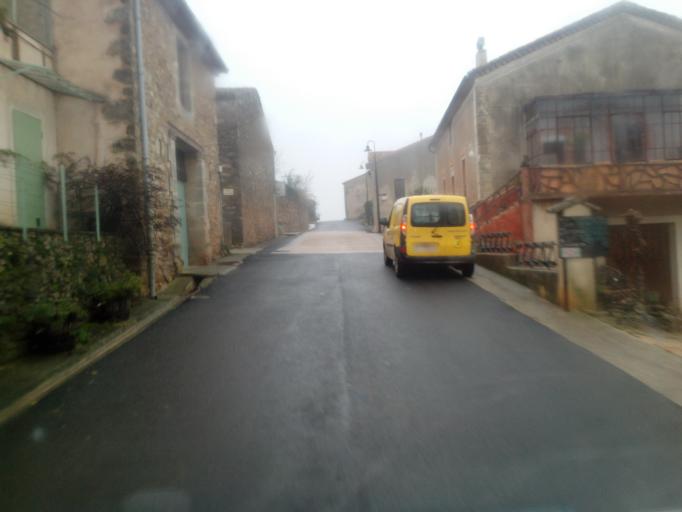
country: FR
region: Languedoc-Roussillon
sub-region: Departement de l'Herault
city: Nebian
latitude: 43.6352
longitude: 3.3713
